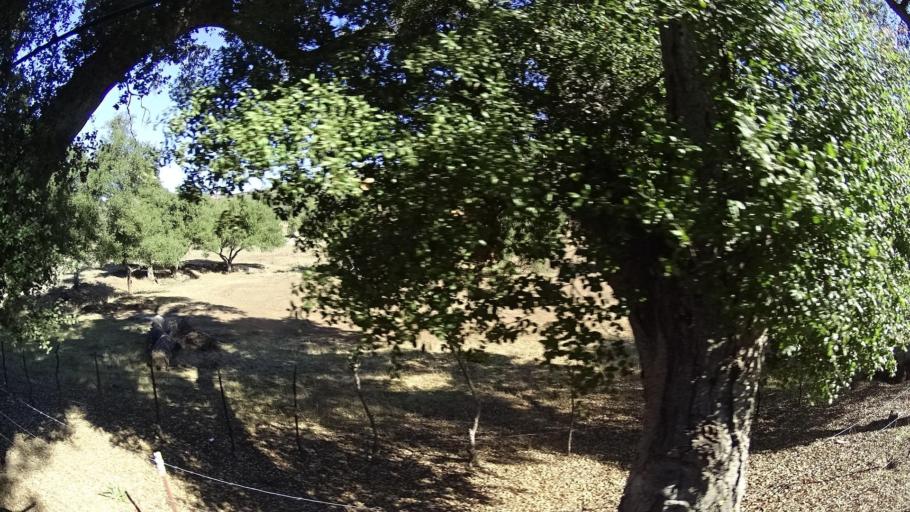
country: US
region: California
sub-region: San Diego County
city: Alpine
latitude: 32.7131
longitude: -116.7528
